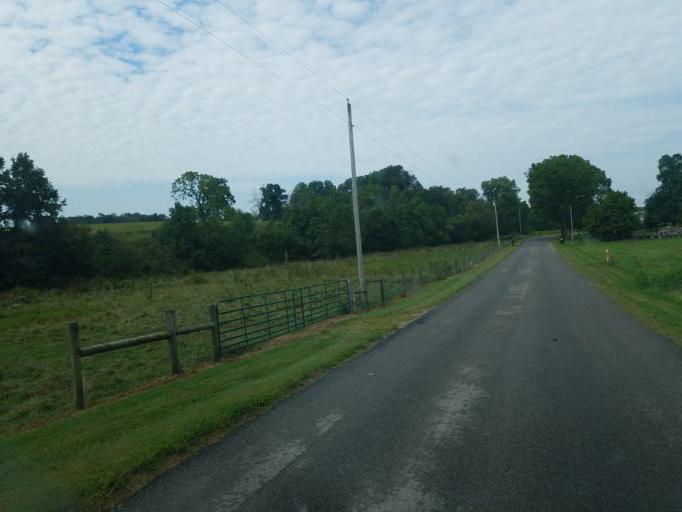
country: US
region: Ohio
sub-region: Morrow County
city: Mount Gilead
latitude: 40.4748
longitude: -82.7327
